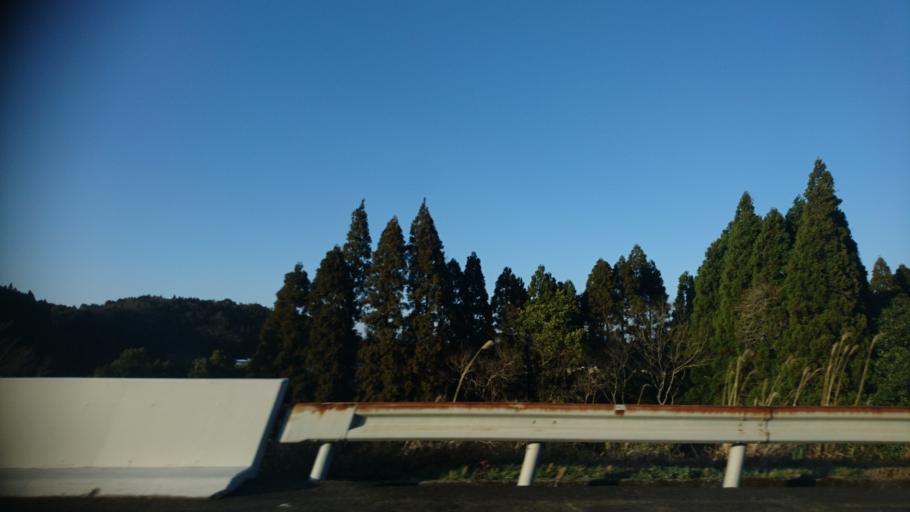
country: JP
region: Miyazaki
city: Miyazaki-shi
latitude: 31.8183
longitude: 131.2662
